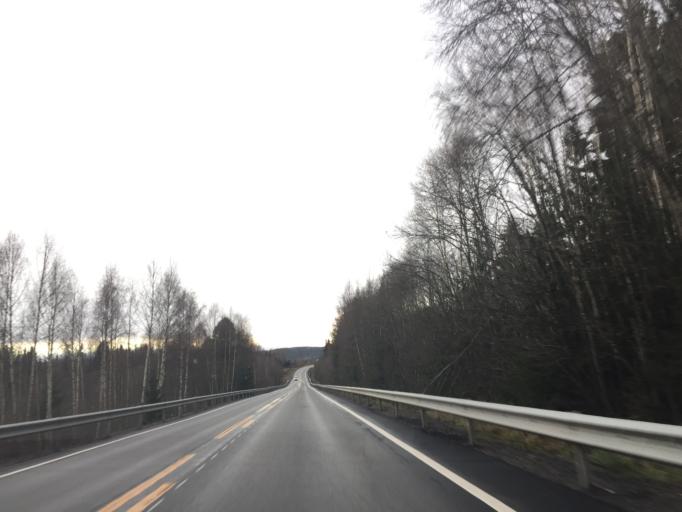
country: NO
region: Hedmark
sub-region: Asnes
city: Flisa
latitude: 60.6175
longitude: 11.9750
